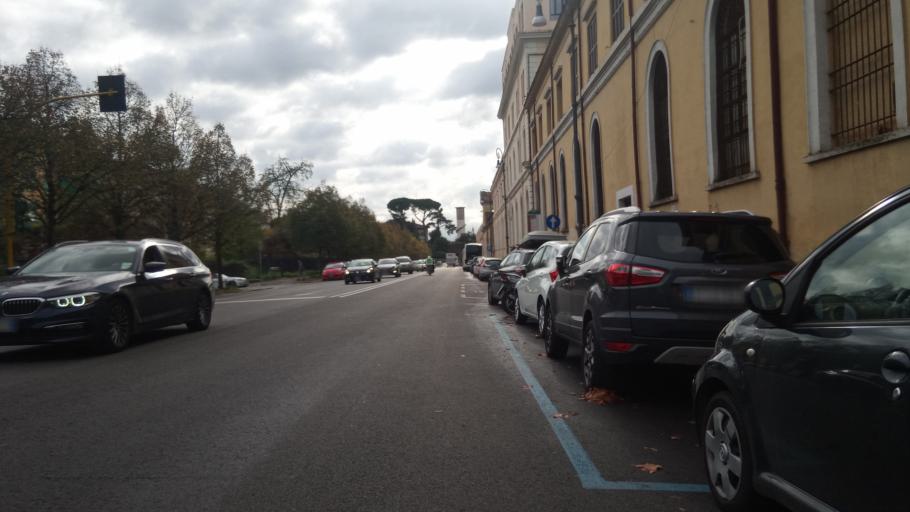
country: IT
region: Latium
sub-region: Citta metropolitana di Roma Capitale
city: Rome
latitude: 41.9010
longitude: 12.5078
